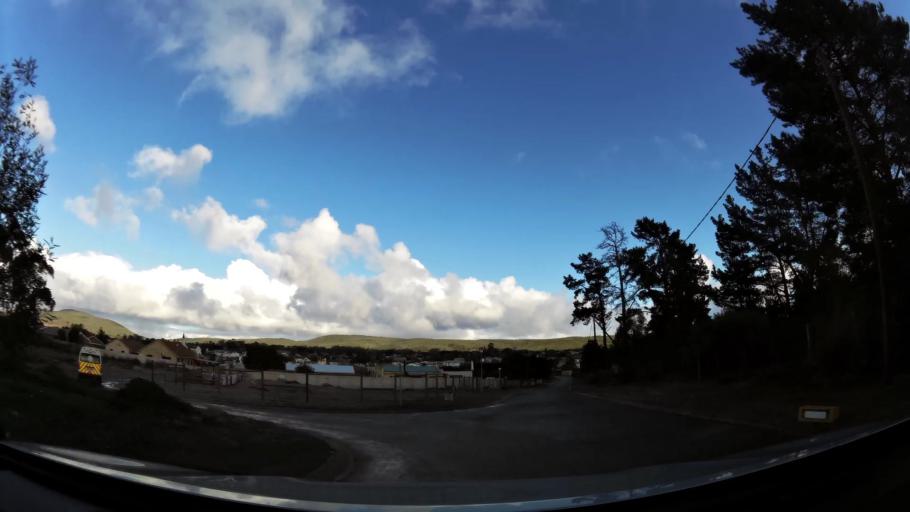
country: ZA
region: Western Cape
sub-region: Eden District Municipality
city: Riversdale
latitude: -34.1990
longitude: 21.5821
